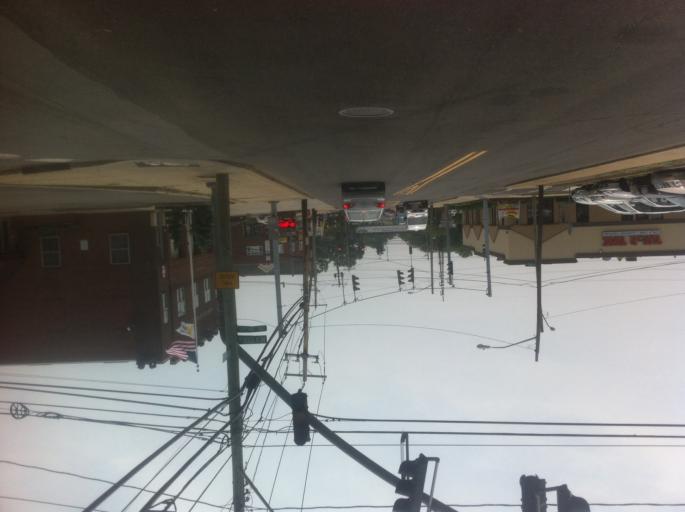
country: US
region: New York
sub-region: Nassau County
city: Massapequa
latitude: 40.6816
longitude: -73.4747
